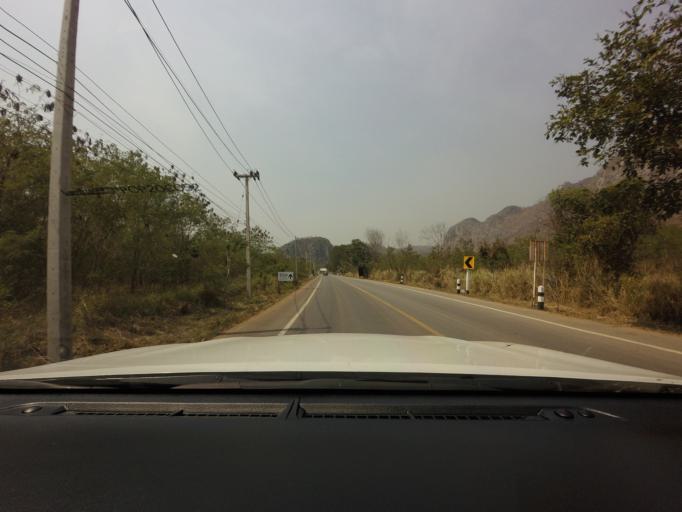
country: TH
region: Sara Buri
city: Muak Lek
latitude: 14.5851
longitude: 101.2515
